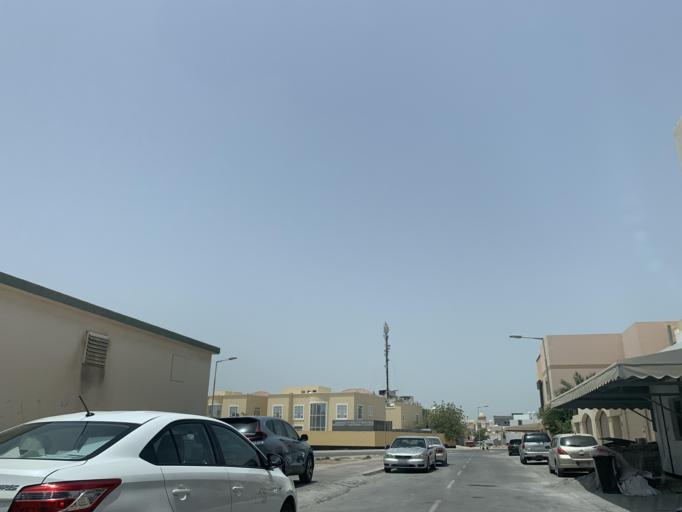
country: BH
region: Northern
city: Sitrah
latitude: 26.1476
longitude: 50.5882
